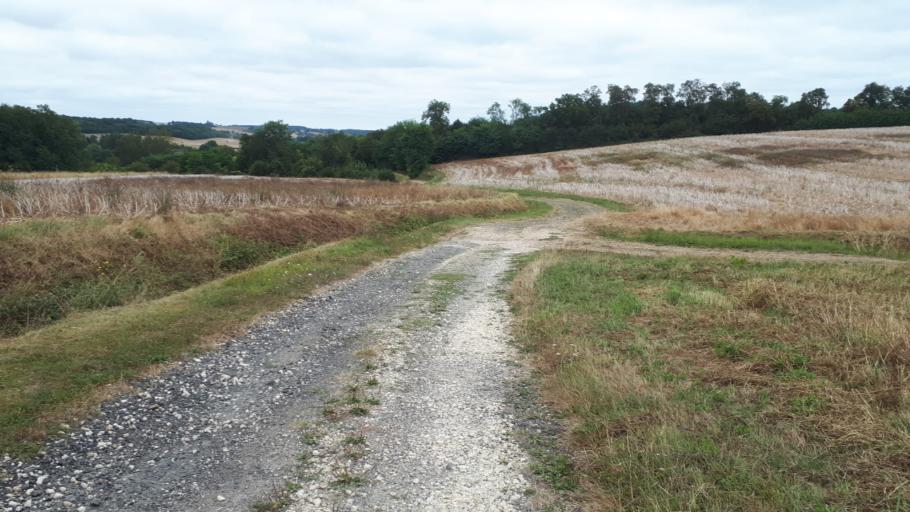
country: FR
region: Centre
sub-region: Departement du Loir-et-Cher
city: Villiers-sur-Loir
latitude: 47.8254
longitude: 0.9826
